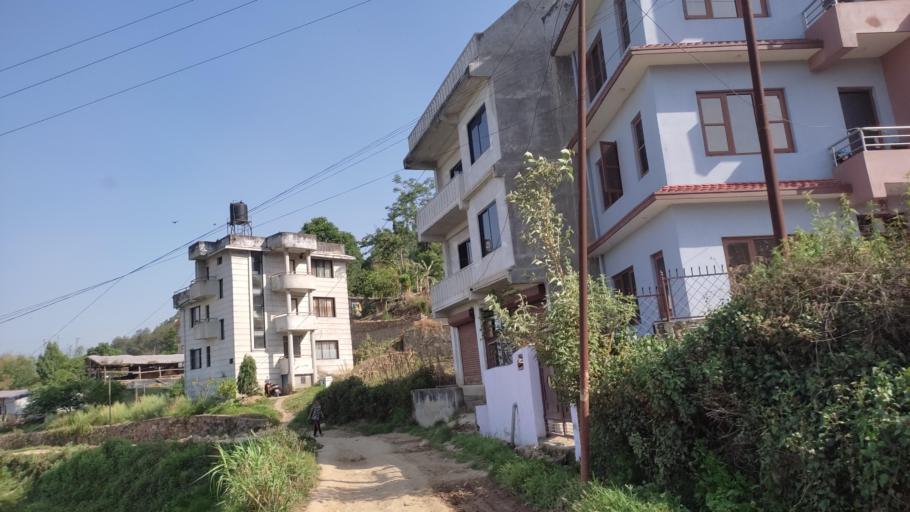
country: NP
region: Central Region
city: Kirtipur
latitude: 27.6605
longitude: 85.2602
